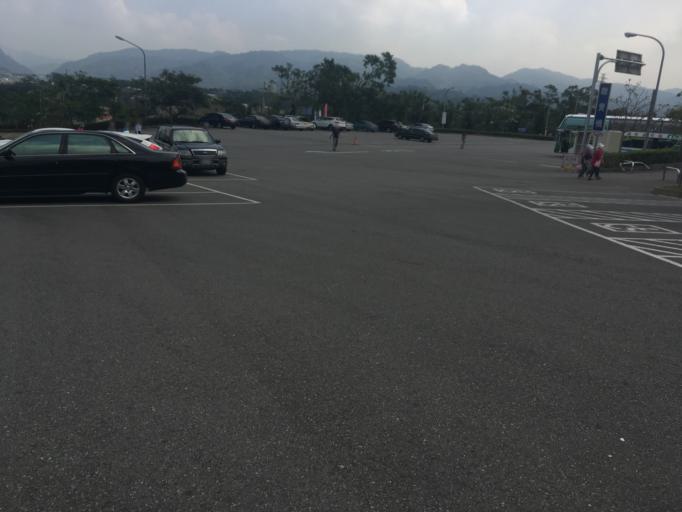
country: TW
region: Taiwan
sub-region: Miaoli
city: Miaoli
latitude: 24.4720
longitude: 120.8039
